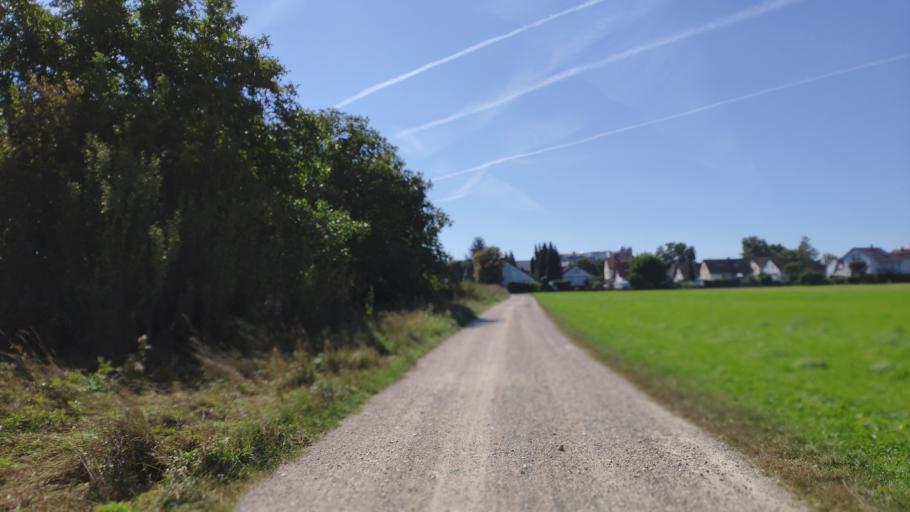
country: DE
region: Bavaria
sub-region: Swabia
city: Senden
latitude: 48.3534
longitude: 10.0365
